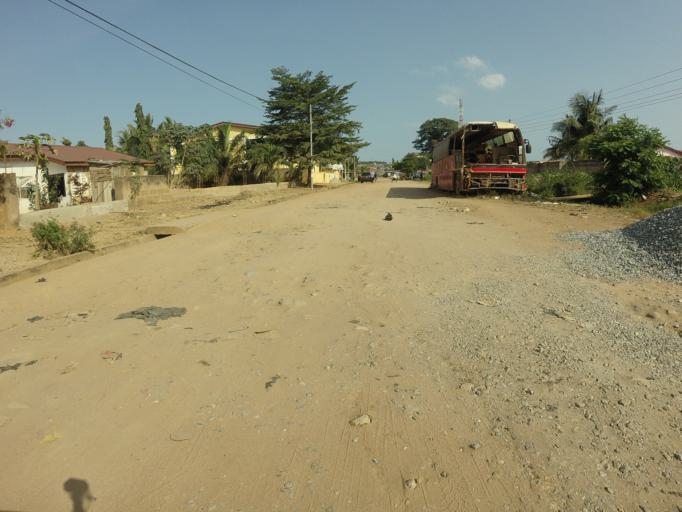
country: GH
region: Greater Accra
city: Dome
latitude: 5.6510
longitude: -0.2624
